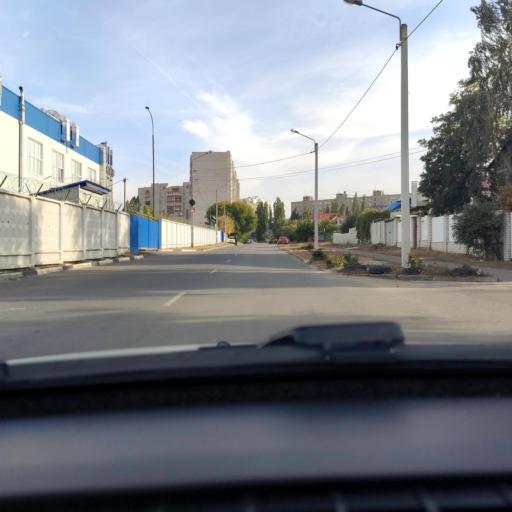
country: RU
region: Voronezj
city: Pridonskoy
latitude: 51.6603
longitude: 39.1255
